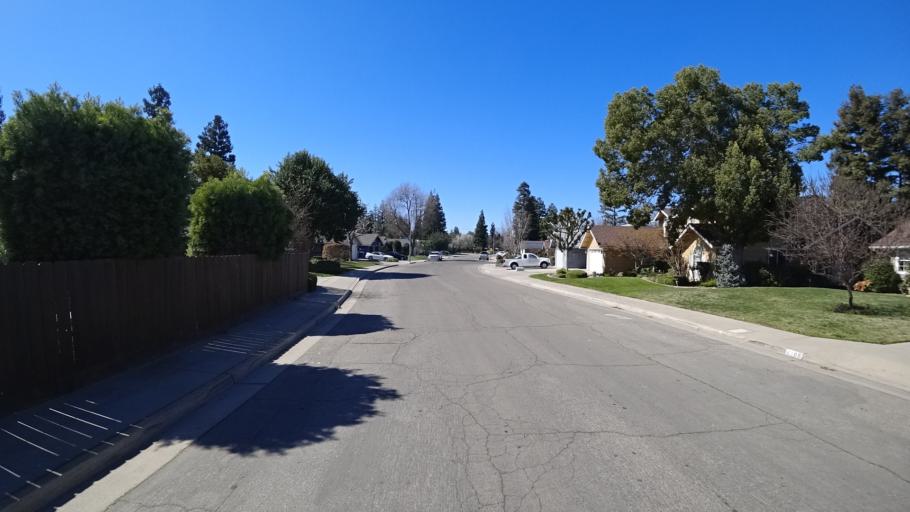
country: US
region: California
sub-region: Fresno County
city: Clovis
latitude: 36.8480
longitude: -119.7638
